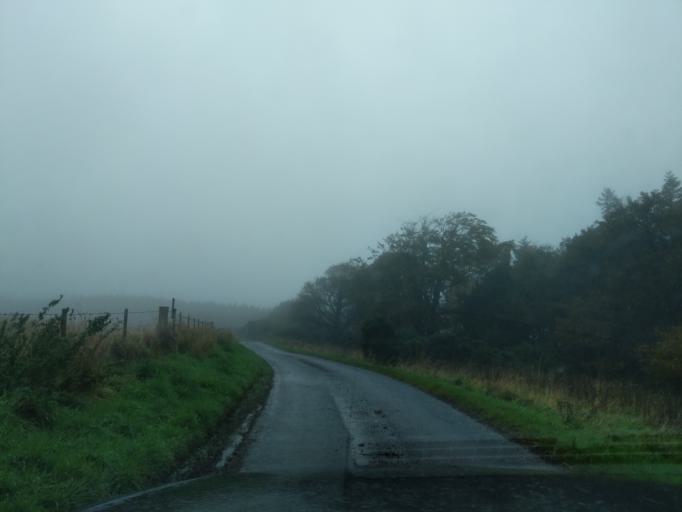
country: GB
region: Scotland
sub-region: East Lothian
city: Dunbar
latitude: 55.9393
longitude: -2.4215
